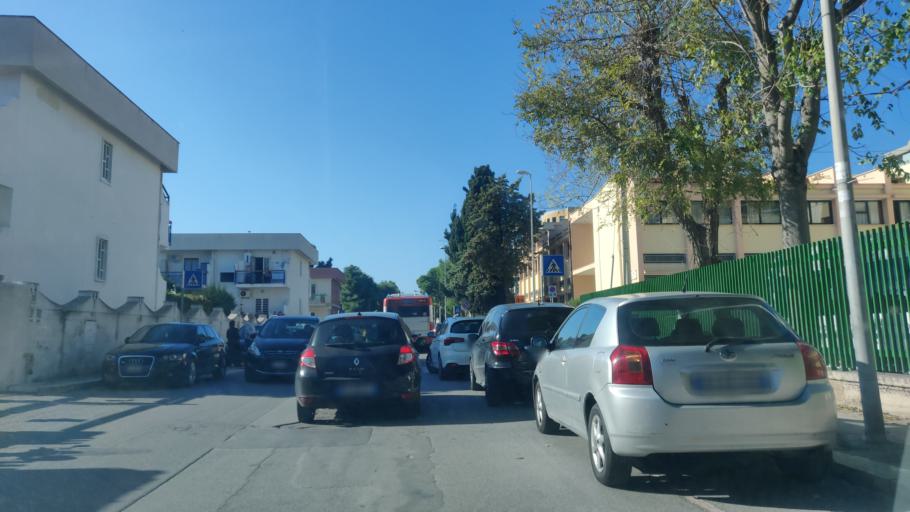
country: IT
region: Apulia
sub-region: Provincia di Bari
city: San Paolo
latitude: 41.1362
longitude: 16.8211
